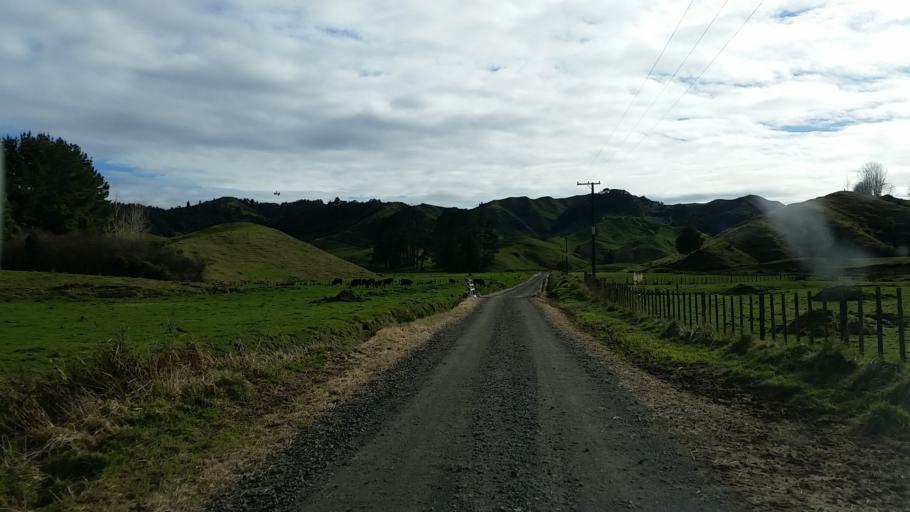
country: NZ
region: Taranaki
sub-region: South Taranaki District
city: Eltham
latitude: -39.2297
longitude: 174.5654
